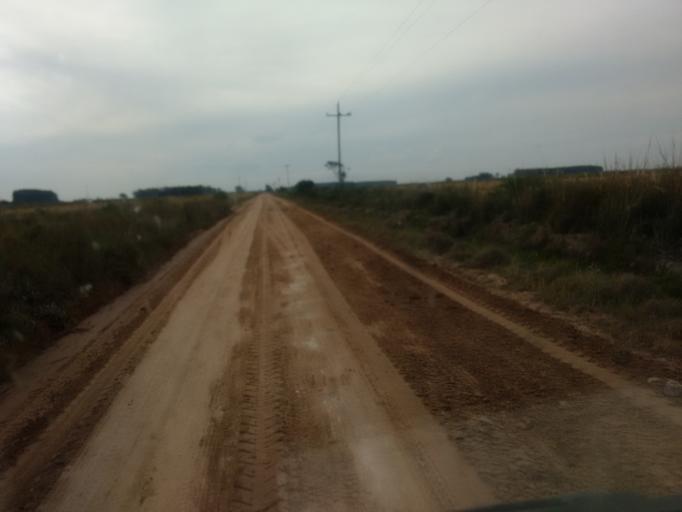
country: BR
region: Rio Grande do Sul
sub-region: Sao Lourenco Do Sul
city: Sao Lourenco do Sul
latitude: -31.1659
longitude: -51.7477
